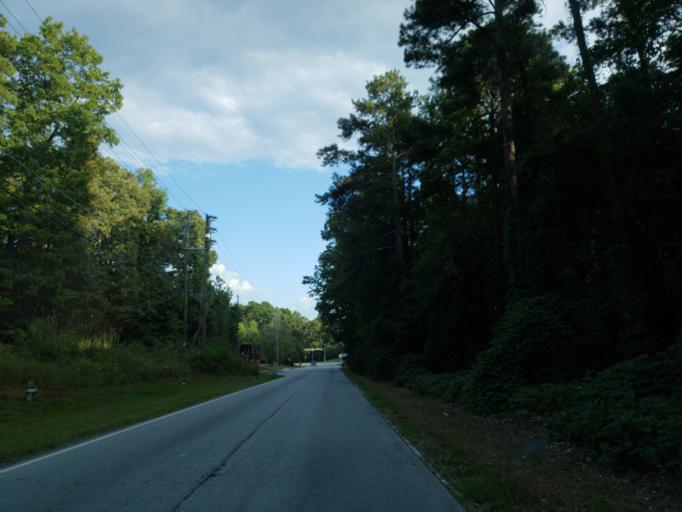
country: US
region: Georgia
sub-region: Cobb County
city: Mableton
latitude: 33.7532
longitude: -84.5825
